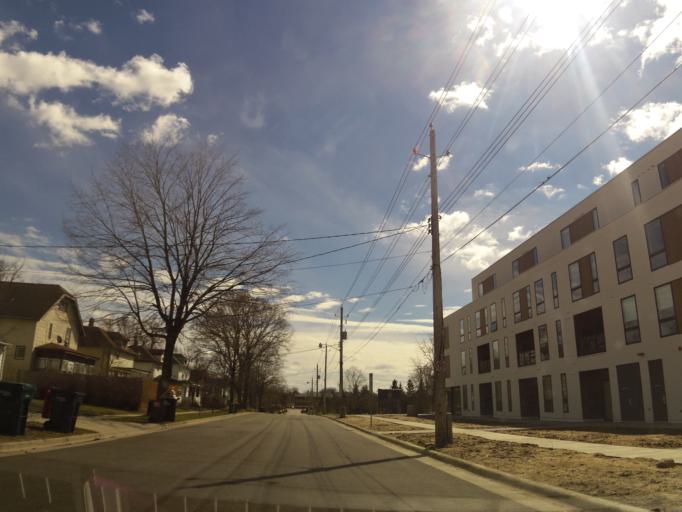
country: US
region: Minnesota
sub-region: Olmsted County
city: Rochester
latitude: 44.0222
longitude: -92.4551
